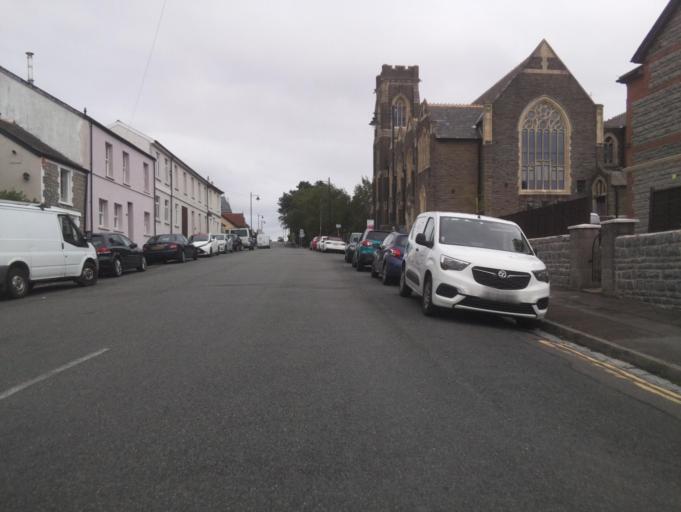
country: GB
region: Wales
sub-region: Vale of Glamorgan
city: Penarth
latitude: 51.4399
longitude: -3.1726
